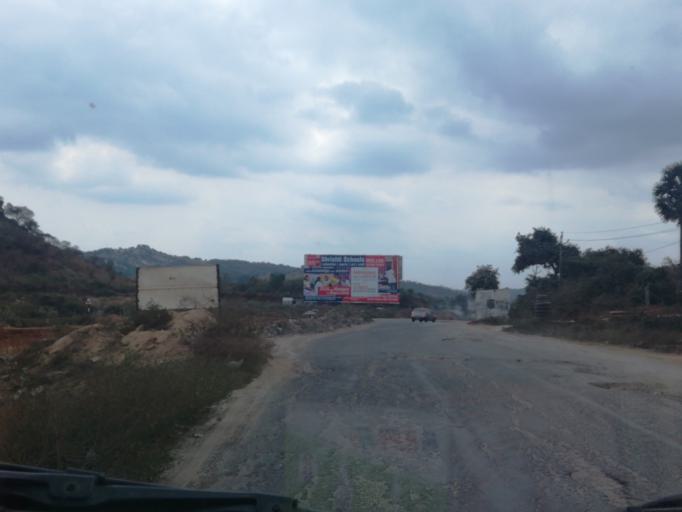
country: IN
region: Andhra Pradesh
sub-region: Chittoor
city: Ramapuram
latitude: 13.0881
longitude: 79.1349
